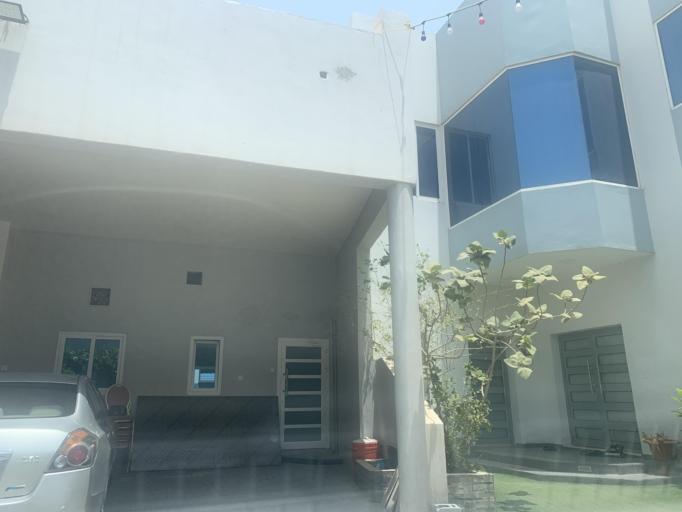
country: BH
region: Manama
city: Jidd Hafs
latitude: 26.2166
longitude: 50.4632
